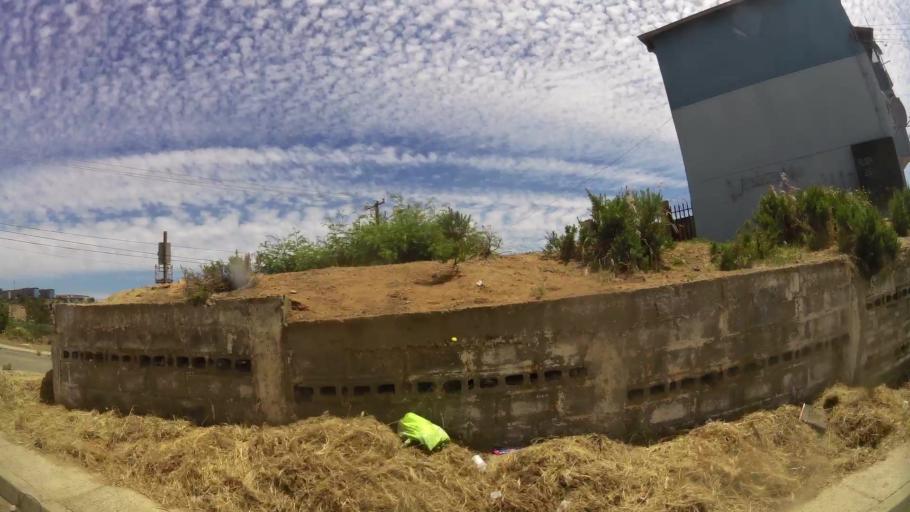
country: CL
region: Valparaiso
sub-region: Provincia de Valparaiso
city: Vina del Mar
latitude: -33.0574
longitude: -71.5661
